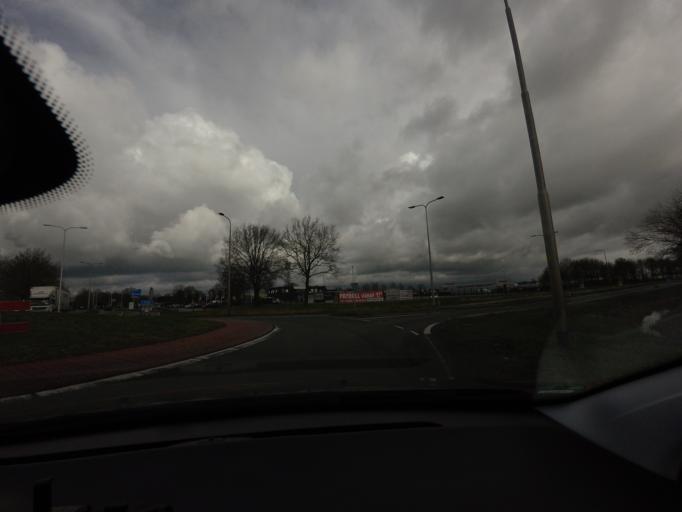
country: NL
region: Overijssel
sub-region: Gemeente Staphorst
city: Staphorst
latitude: 52.6854
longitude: 6.2684
